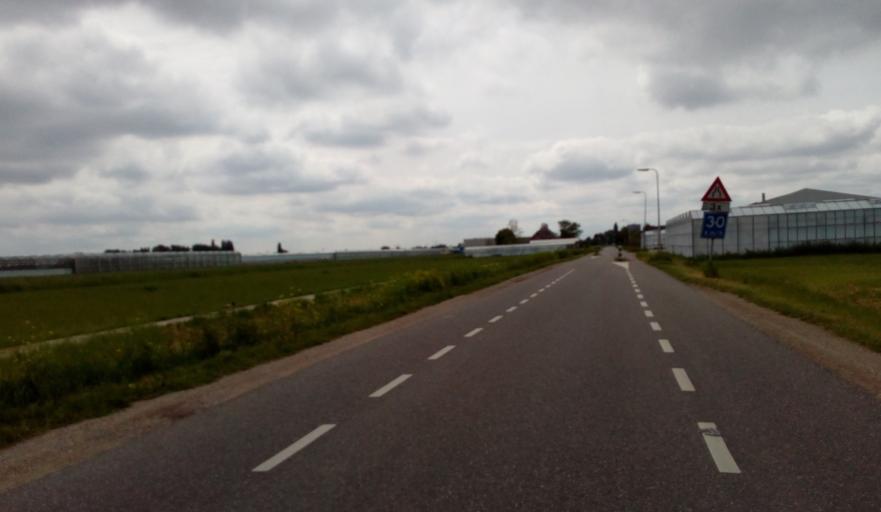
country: NL
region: South Holland
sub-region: Gemeente Waddinxveen
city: Waddinxveen
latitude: 51.9938
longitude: 4.6084
